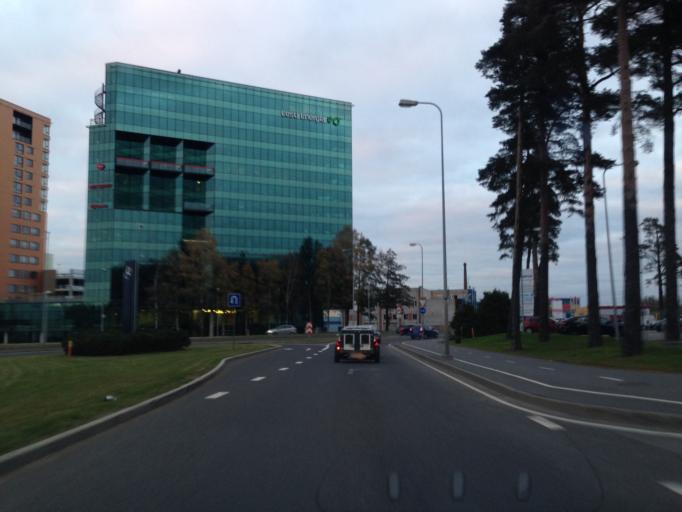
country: EE
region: Harju
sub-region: Tallinna linn
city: Tallinn
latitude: 59.4028
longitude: 24.7334
